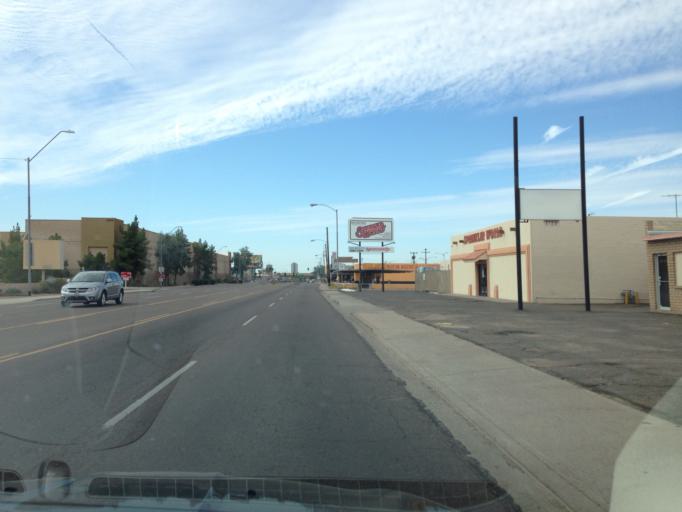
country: US
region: Arizona
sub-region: Maricopa County
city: Phoenix
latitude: 33.4949
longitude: -112.0356
